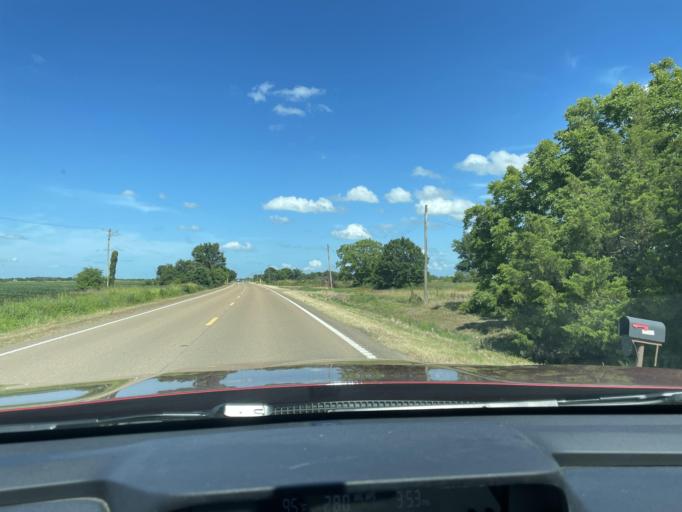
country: US
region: Mississippi
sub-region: Washington County
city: Hollandale
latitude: 33.1843
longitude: -90.6773
